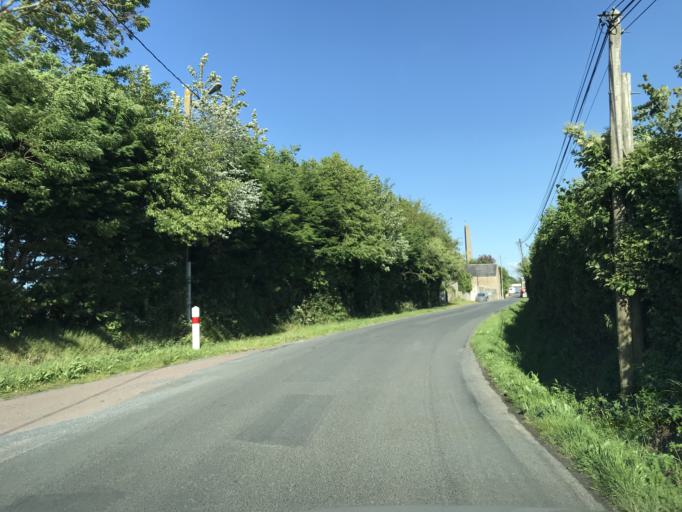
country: FR
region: Lower Normandy
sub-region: Departement du Calvados
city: Grandcamp-Maisy
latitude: 49.3818
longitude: -1.0598
